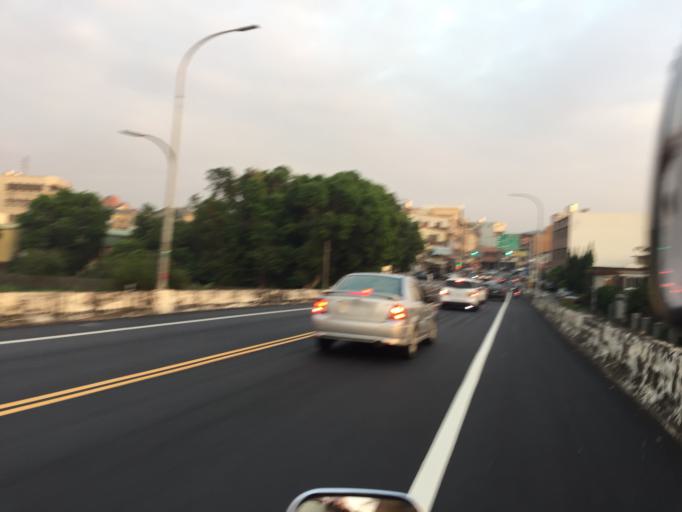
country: TW
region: Taiwan
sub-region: Miaoli
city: Miaoli
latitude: 24.4924
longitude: 120.7873
